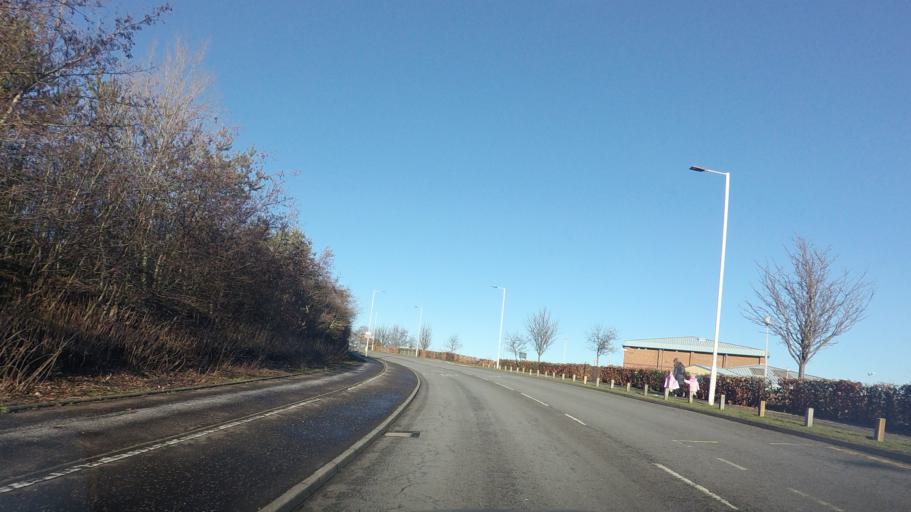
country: GB
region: Scotland
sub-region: Fife
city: Inverkeithing
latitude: 56.0376
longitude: -3.3651
